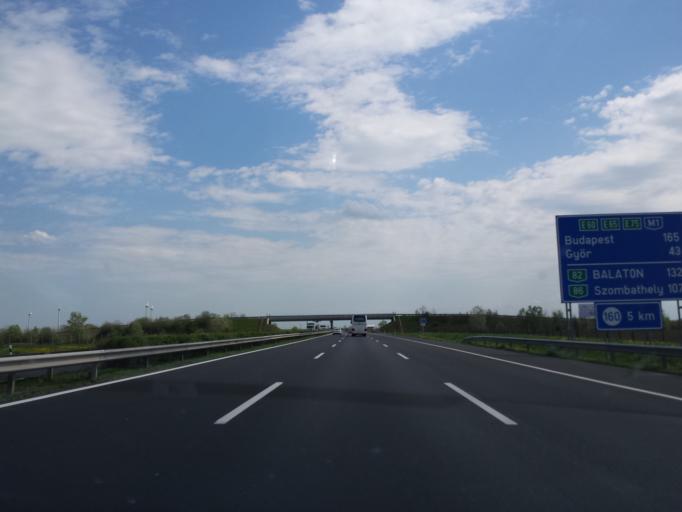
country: HU
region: Gyor-Moson-Sopron
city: Mosonmagyarovar
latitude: 47.8849
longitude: 17.1906
